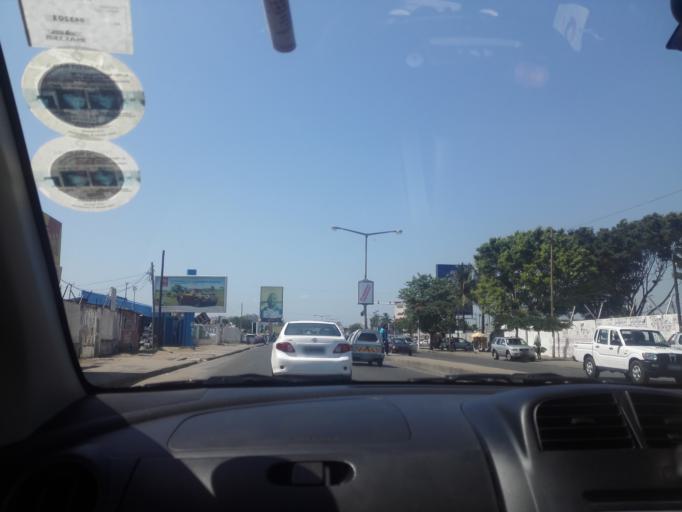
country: MZ
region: Maputo City
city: Maputo
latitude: -25.9458
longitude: 32.5788
